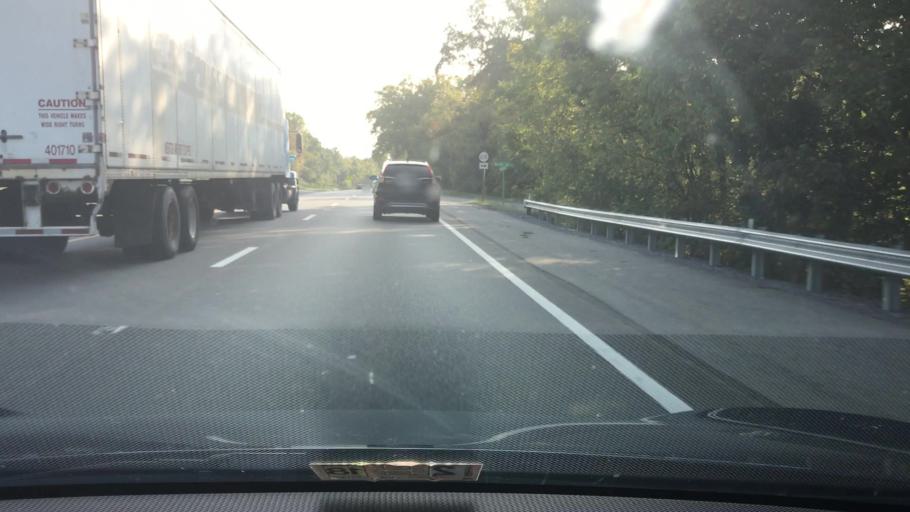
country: US
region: Virginia
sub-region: Botetourt County
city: Laymantown
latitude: 37.3429
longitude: -79.8485
